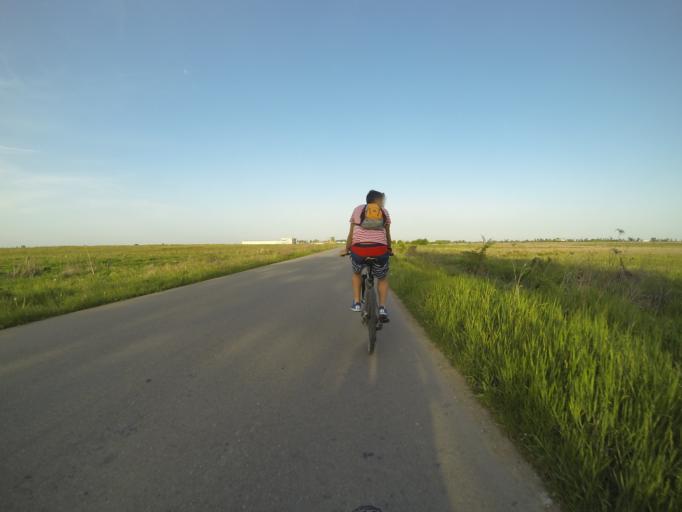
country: RO
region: Dolj
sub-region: Comuna Carcea
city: Carcea
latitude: 44.3225
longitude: 23.8718
